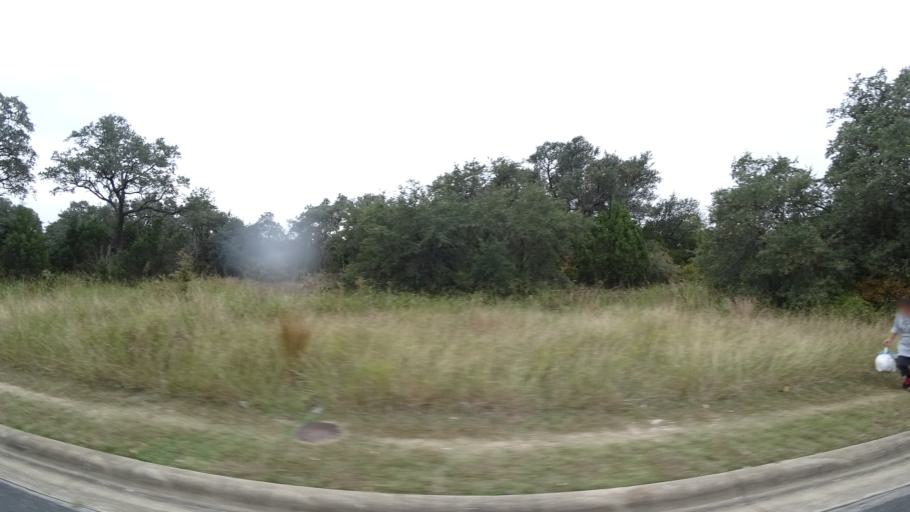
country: US
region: Texas
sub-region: Williamson County
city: Anderson Mill
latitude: 30.4742
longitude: -97.8032
